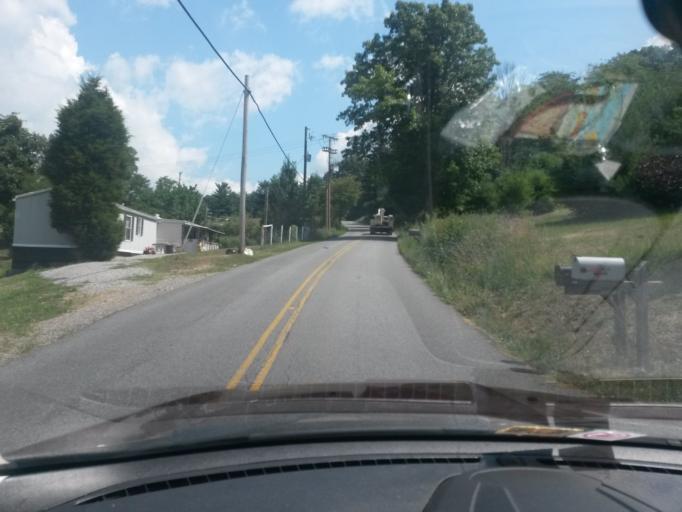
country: US
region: Virginia
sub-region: Giles County
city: Narrows
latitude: 37.3667
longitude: -80.8140
